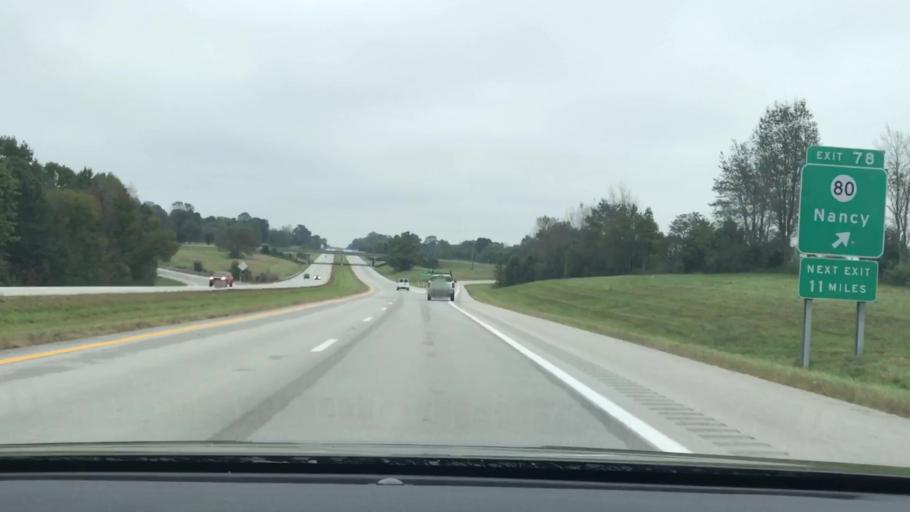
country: US
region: Kentucky
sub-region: Pulaski County
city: Somerset
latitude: 37.0917
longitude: -84.8063
